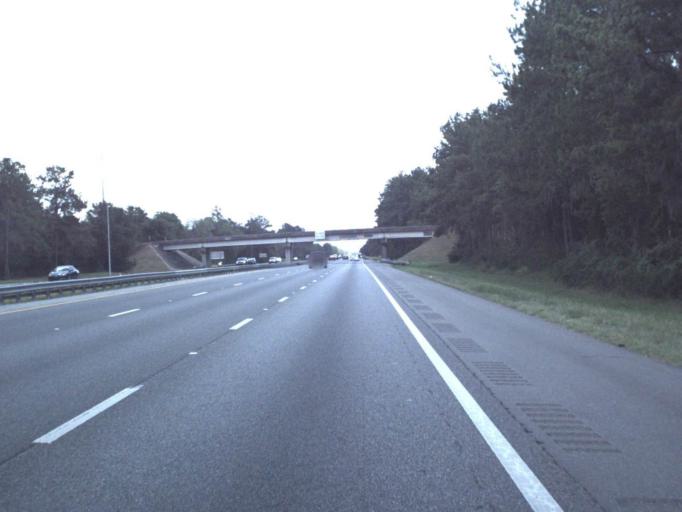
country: US
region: Florida
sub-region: Hamilton County
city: Jasper
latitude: 30.4100
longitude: -82.8929
